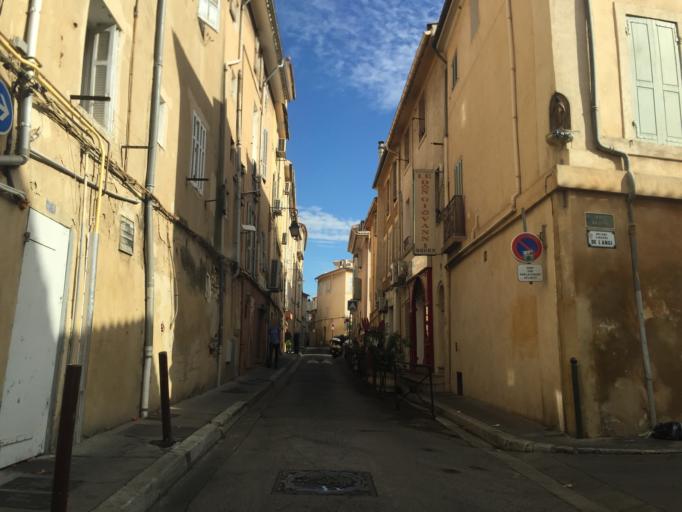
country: FR
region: Provence-Alpes-Cote d'Azur
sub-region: Departement des Bouches-du-Rhone
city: Aix-en-Provence
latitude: 43.5279
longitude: 5.4439
